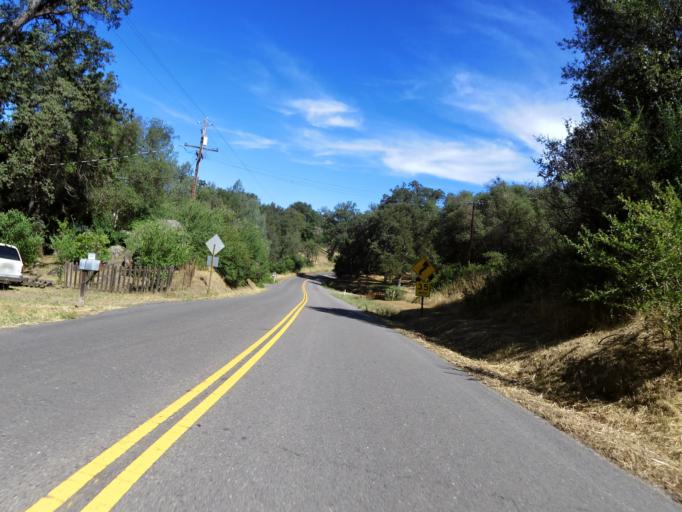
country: US
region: California
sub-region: Mariposa County
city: Mariposa
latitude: 37.4536
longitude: -119.9448
